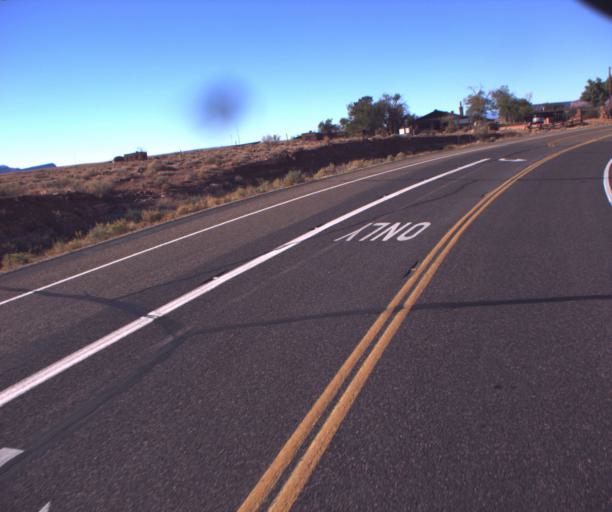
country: US
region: Arizona
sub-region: Coconino County
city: Page
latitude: 36.8168
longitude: -111.6364
